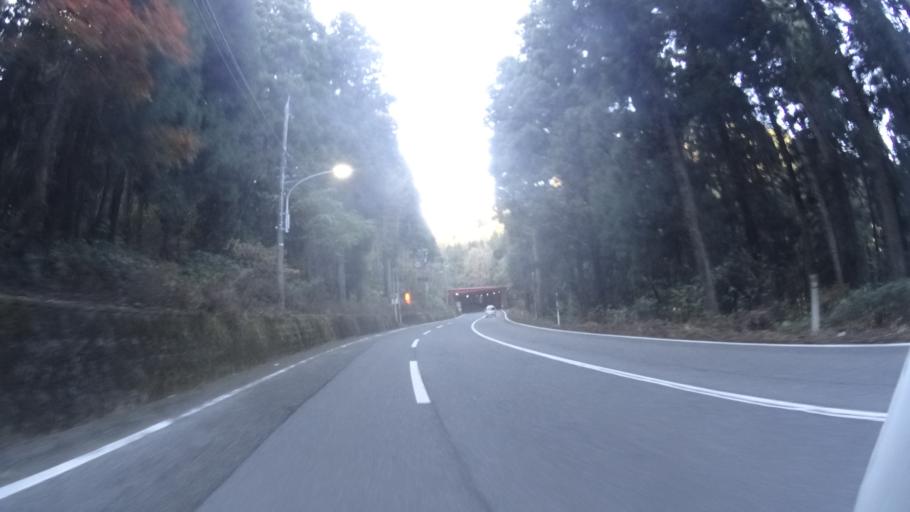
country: JP
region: Fukui
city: Ono
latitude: 35.9976
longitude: 136.4556
